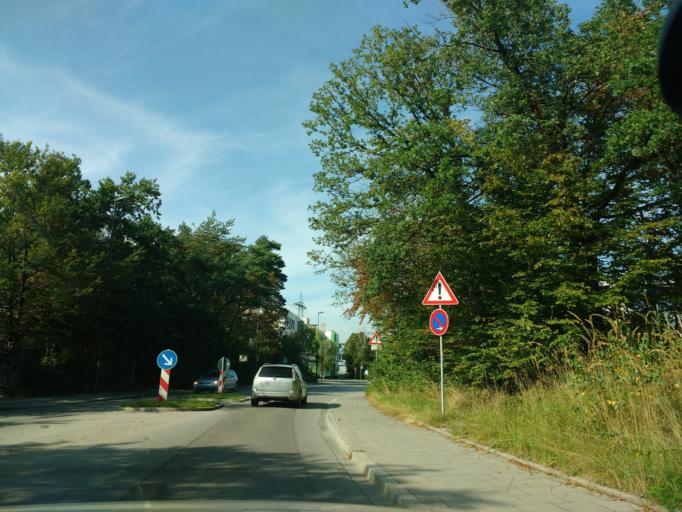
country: DE
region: Bavaria
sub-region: Upper Bavaria
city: Grafelfing
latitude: 48.1194
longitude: 11.4504
